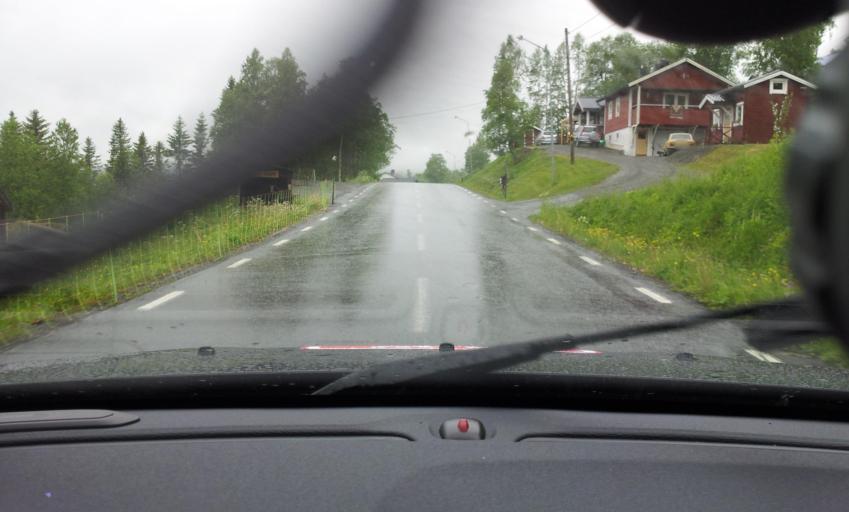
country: SE
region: Jaemtland
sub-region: Are Kommun
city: Are
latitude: 63.3152
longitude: 13.0835
